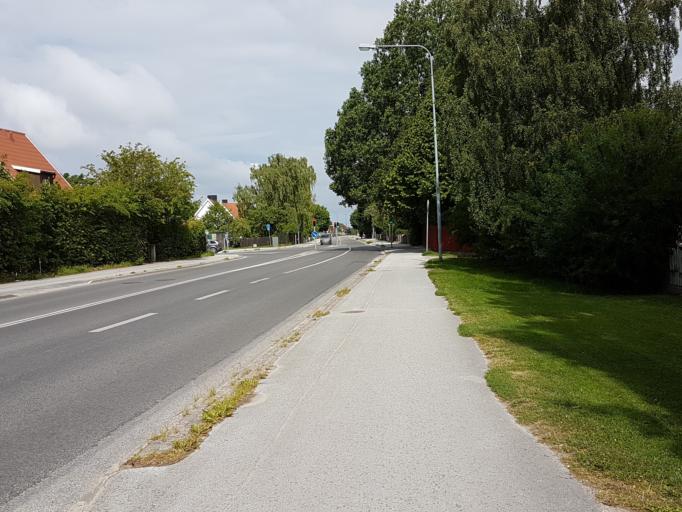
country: SE
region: Gotland
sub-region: Gotland
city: Visby
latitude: 57.6324
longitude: 18.3116
